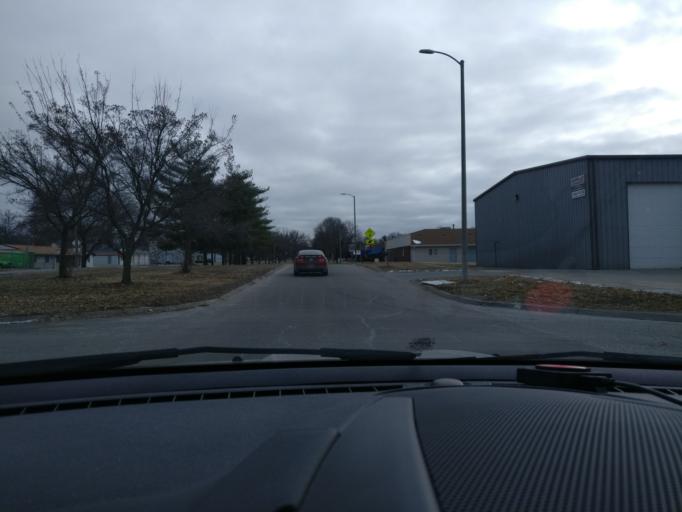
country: US
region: Nebraska
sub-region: Lancaster County
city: Lincoln
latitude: 40.8518
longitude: -96.6402
